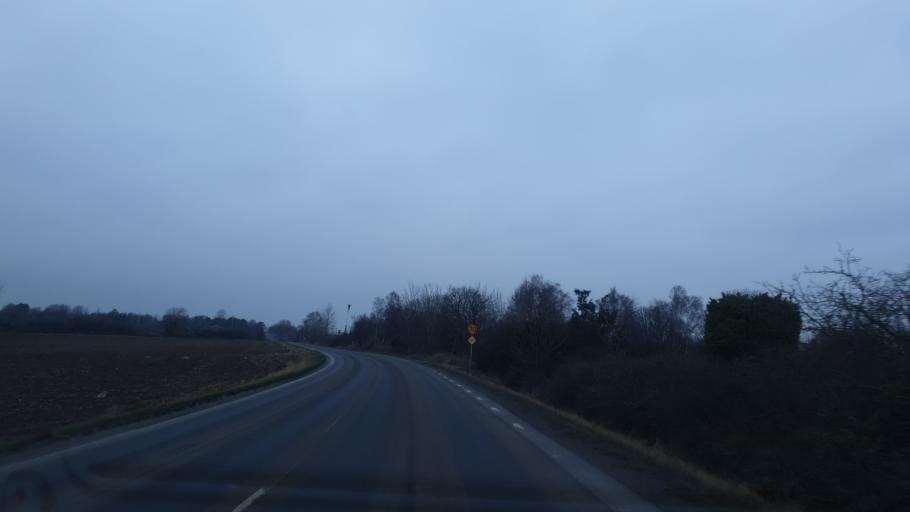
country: SE
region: Blekinge
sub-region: Karlskrona Kommun
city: Jaemjoe
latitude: 56.1436
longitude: 15.7563
